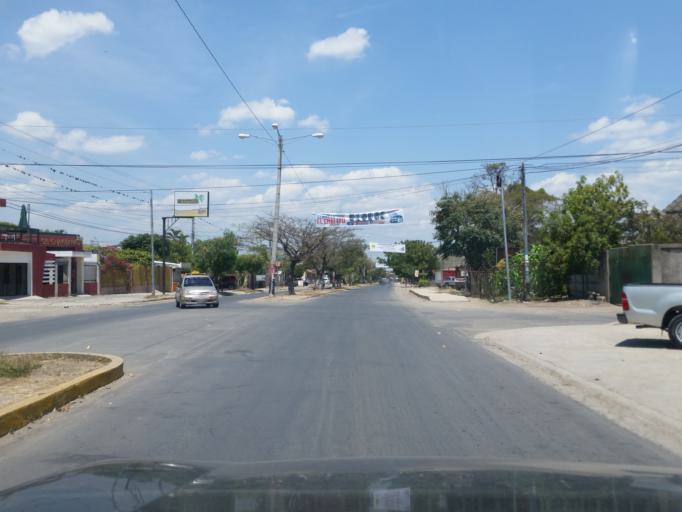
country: NI
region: Esteli
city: Esteli
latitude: 13.0750
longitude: -86.3538
